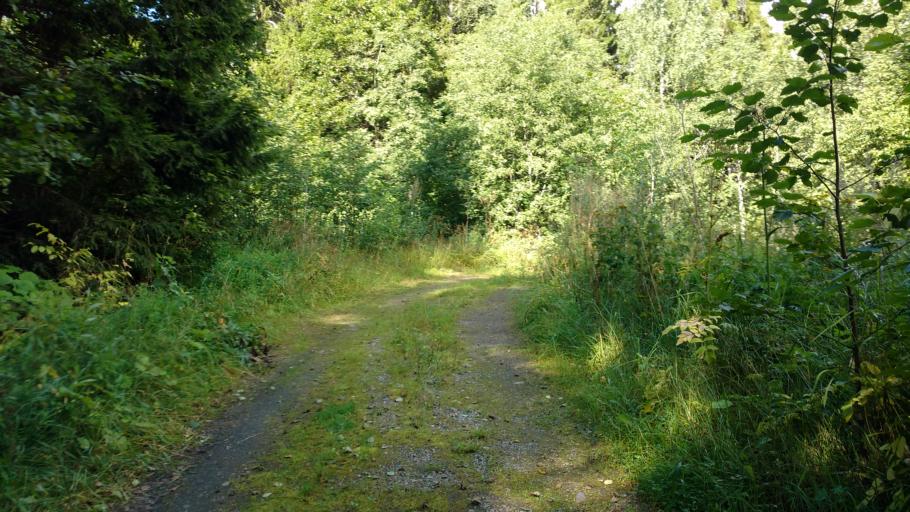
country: FI
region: Varsinais-Suomi
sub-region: Salo
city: Salo
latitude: 60.3517
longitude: 23.1368
